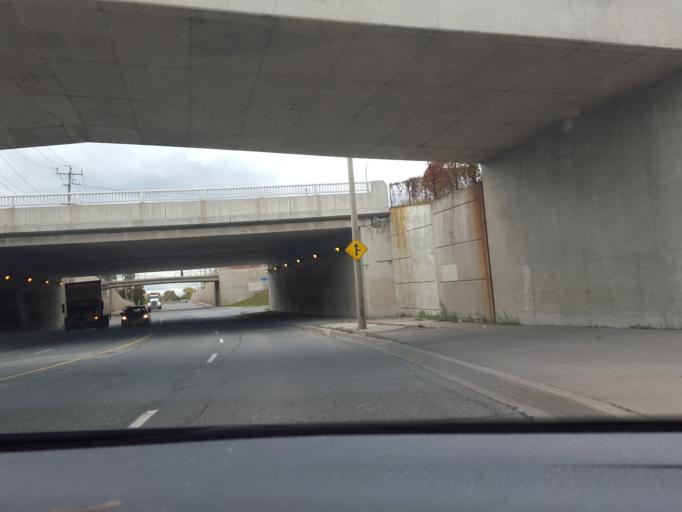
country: CA
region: Ontario
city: Etobicoke
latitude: 43.6304
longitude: -79.5522
